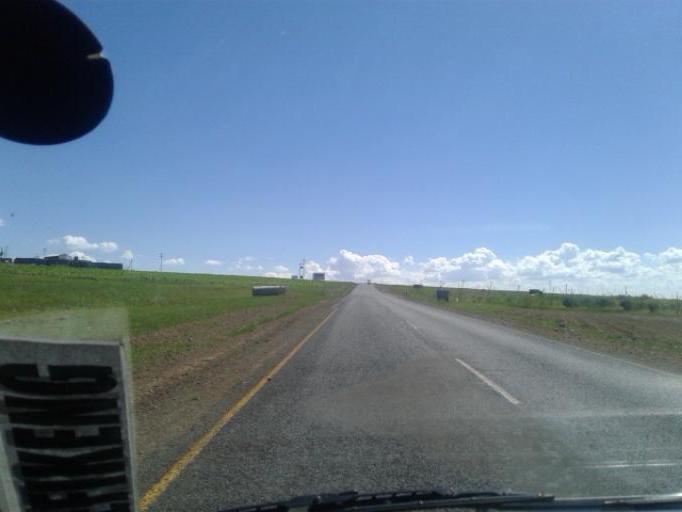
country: LS
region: Maseru
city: Maseru
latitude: -29.3064
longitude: 27.6059
